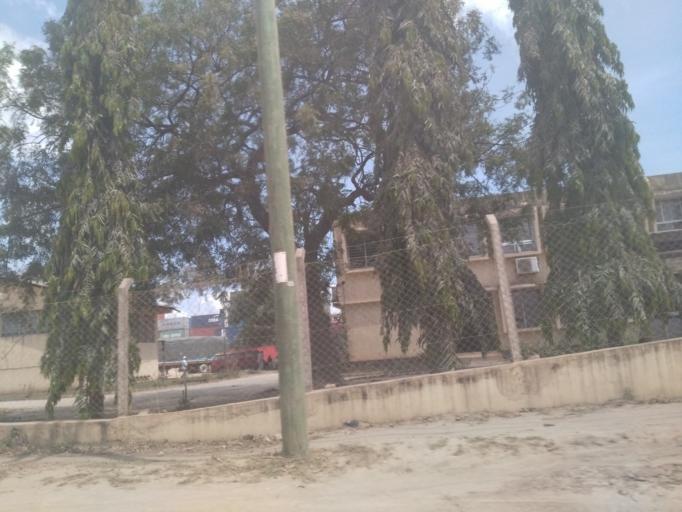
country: TZ
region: Dar es Salaam
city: Dar es Salaam
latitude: -6.8424
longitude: 39.2573
